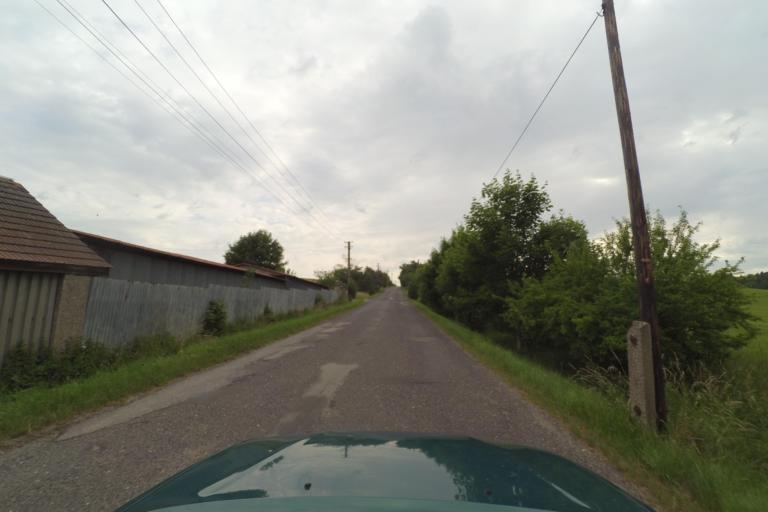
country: CZ
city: Cesky Dub
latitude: 50.6614
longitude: 15.0059
